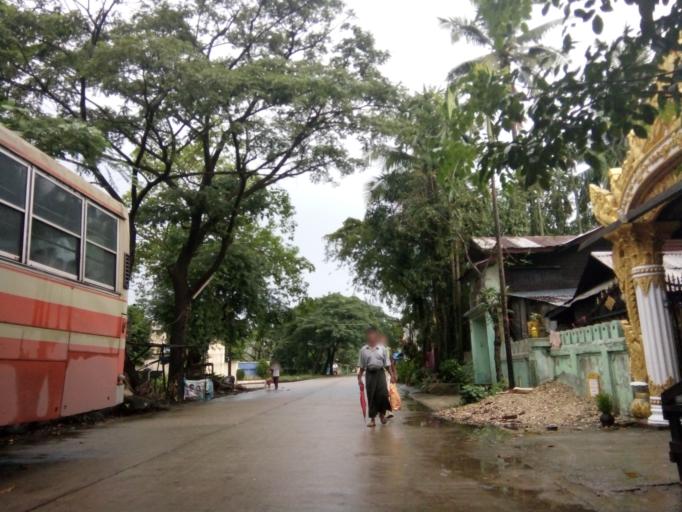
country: MM
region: Yangon
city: Yangon
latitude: 16.9189
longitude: 96.1585
